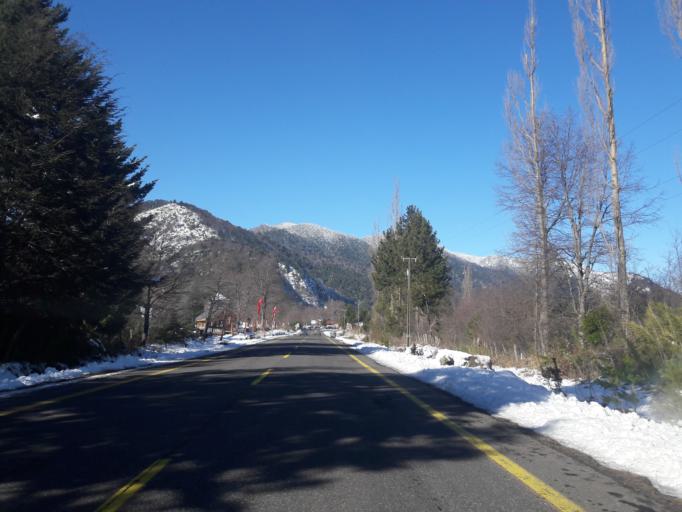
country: CL
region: Araucania
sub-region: Provincia de Cautin
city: Vilcun
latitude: -38.4779
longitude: -71.5400
